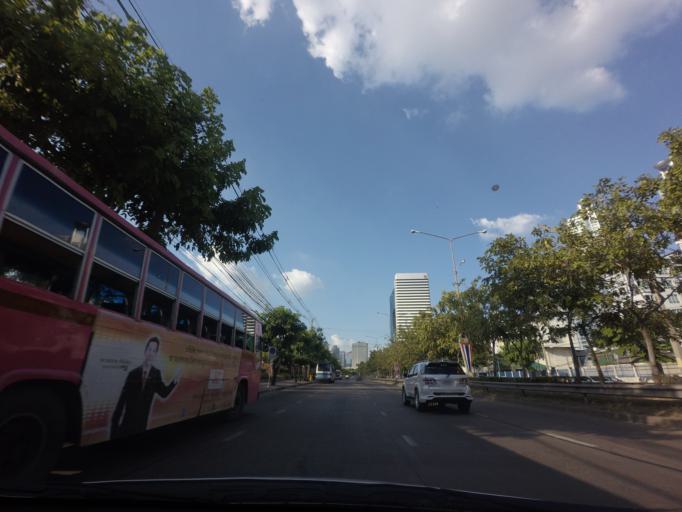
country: TH
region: Bangkok
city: Khlong Toei
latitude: 13.7274
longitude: 100.5601
